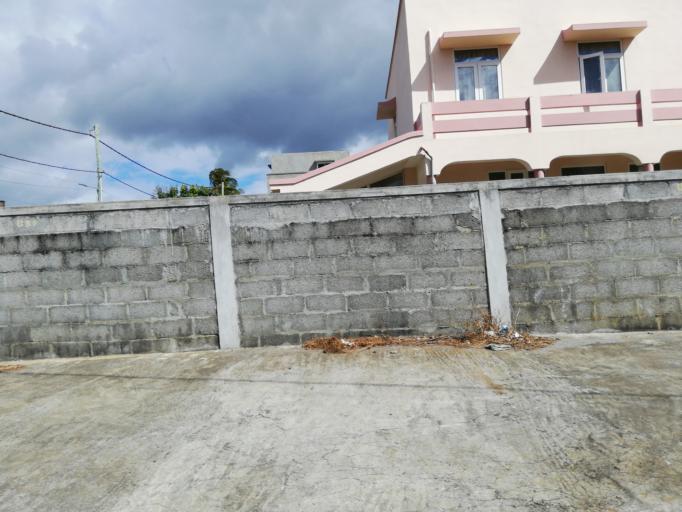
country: MU
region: Moka
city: Moka
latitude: -20.2205
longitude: 57.4753
